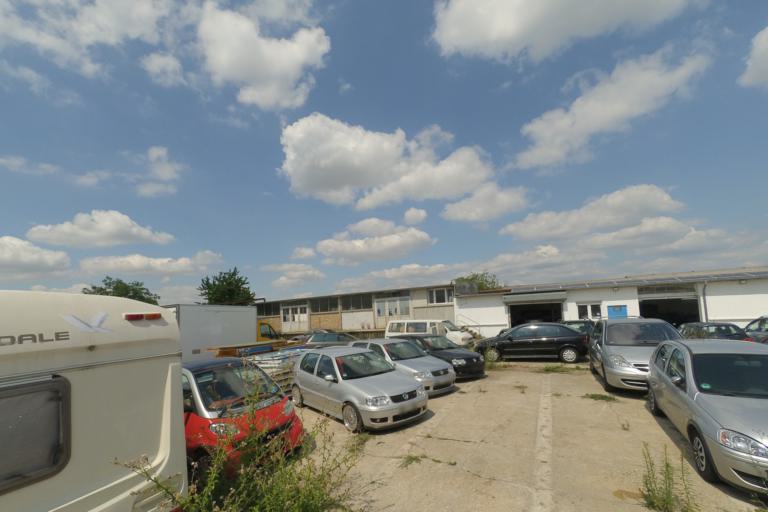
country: DE
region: Rheinland-Pfalz
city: Frankenthal
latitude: 49.5220
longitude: 8.3923
